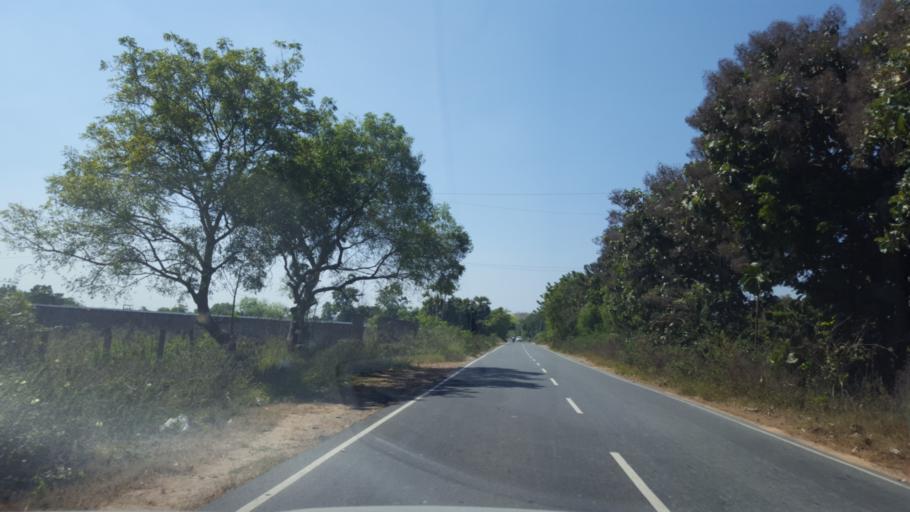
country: IN
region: Tamil Nadu
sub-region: Kancheepuram
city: Wallajahbad
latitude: 12.7707
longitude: 79.8962
